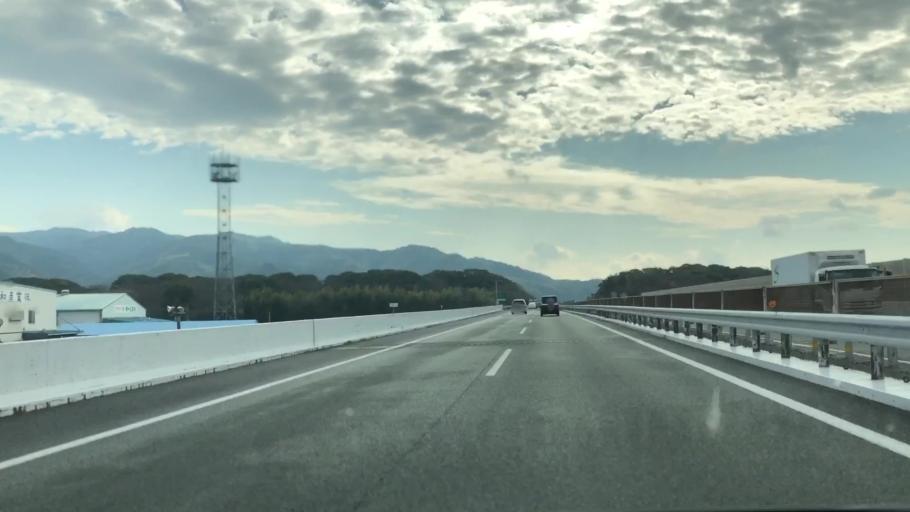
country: JP
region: Fukuoka
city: Setakamachi-takayanagi
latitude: 33.1853
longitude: 130.5188
